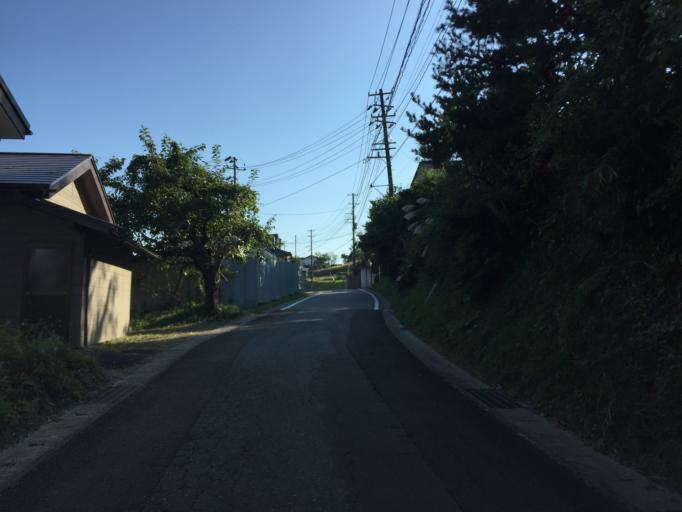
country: JP
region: Fukushima
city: Fukushima-shi
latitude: 37.7085
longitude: 140.4650
